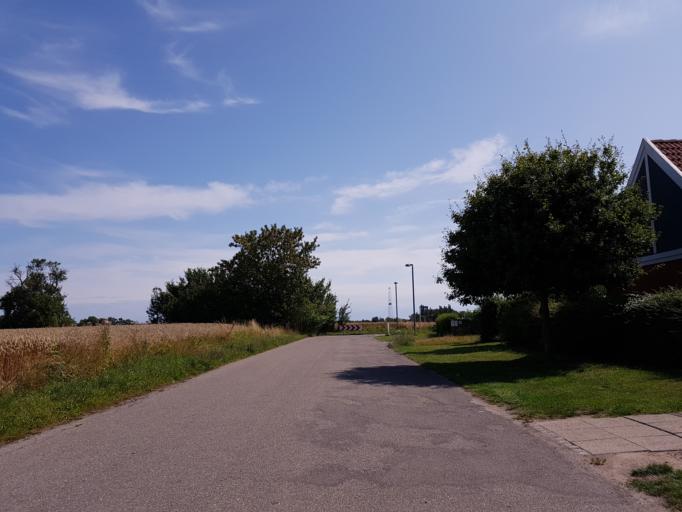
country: DK
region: Zealand
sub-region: Guldborgsund Kommune
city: Nykobing Falster
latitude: 54.5763
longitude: 11.9358
